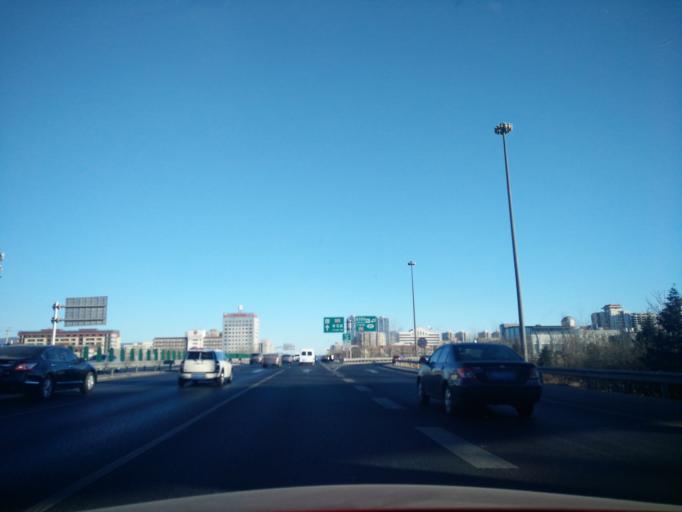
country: CN
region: Beijing
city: Lugu
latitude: 39.8937
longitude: 116.2052
